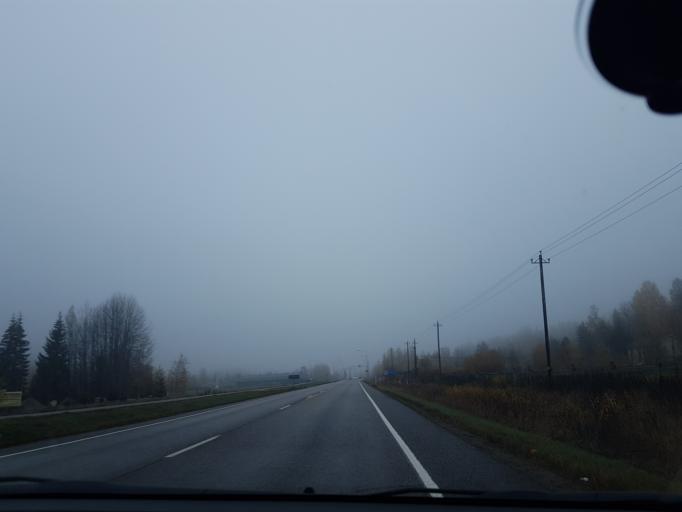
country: FI
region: Uusimaa
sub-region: Helsinki
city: Jaervenpaeae
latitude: 60.4597
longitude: 25.1384
